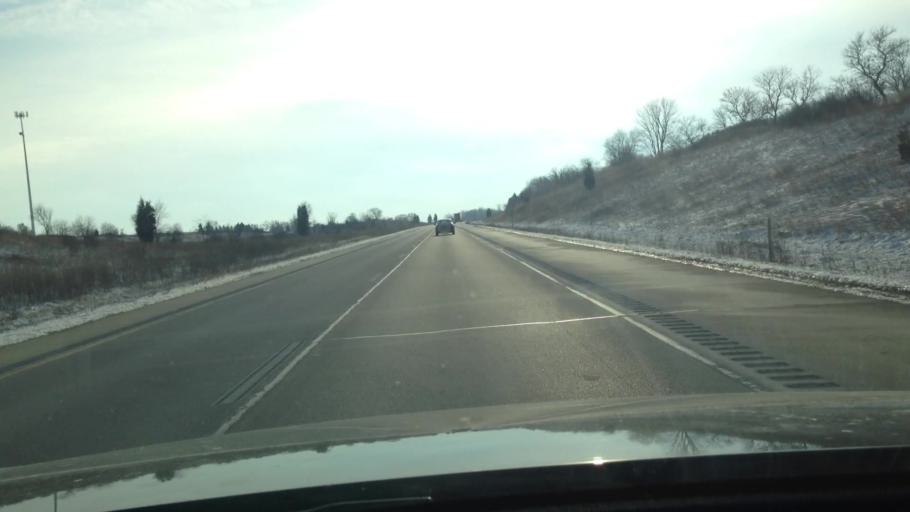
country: US
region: Wisconsin
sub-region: Walworth County
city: East Troy
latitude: 42.7606
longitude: -88.4331
